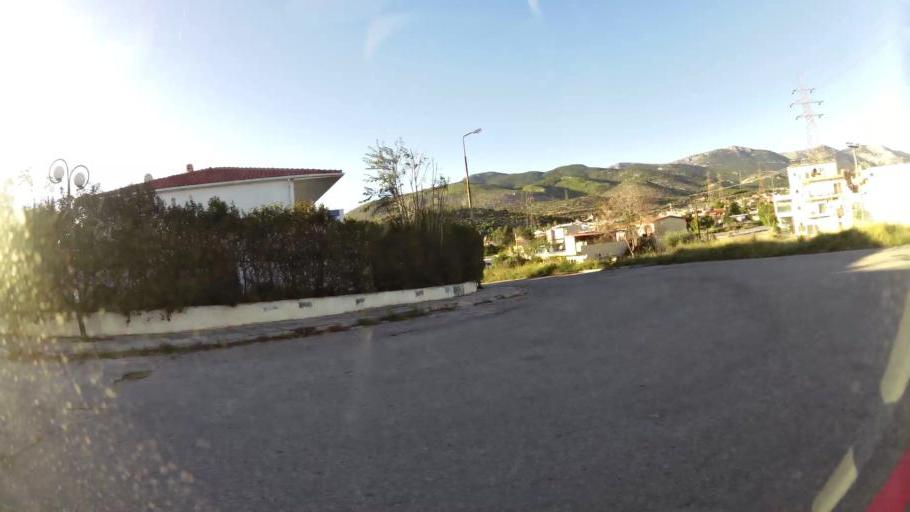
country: GR
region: Attica
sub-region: Nomarchia Anatolikis Attikis
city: Acharnes
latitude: 38.0903
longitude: 23.7206
